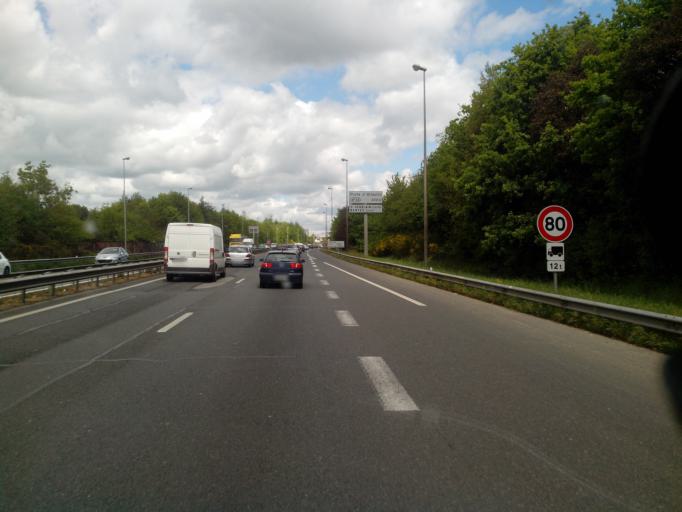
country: FR
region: Pays de la Loire
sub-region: Departement de la Loire-Atlantique
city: Saint-Herblain
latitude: 47.2138
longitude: -1.6260
